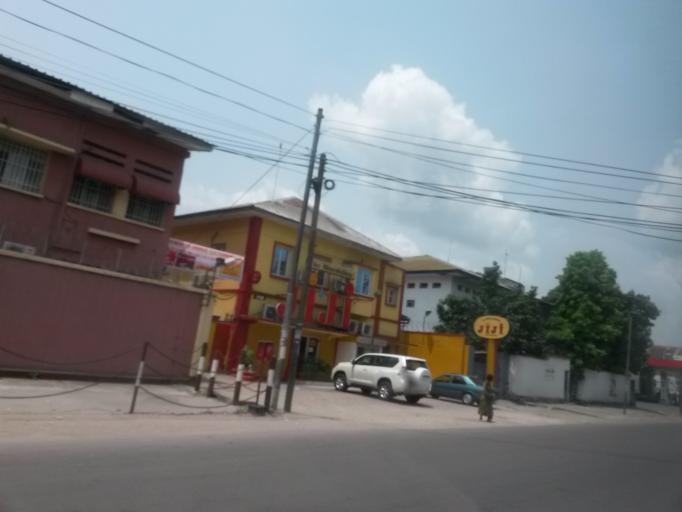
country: CD
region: Kinshasa
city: Kinshasa
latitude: -4.3126
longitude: 15.2896
